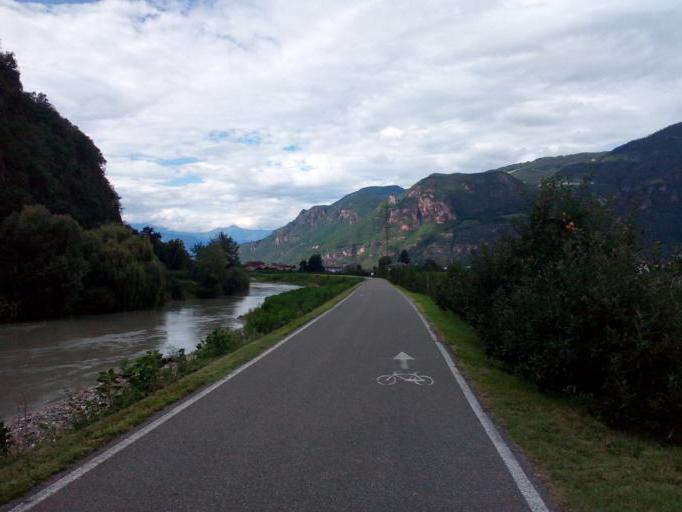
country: IT
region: Trentino-Alto Adige
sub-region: Bolzano
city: Cornaiano
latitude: 46.4798
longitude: 11.3081
